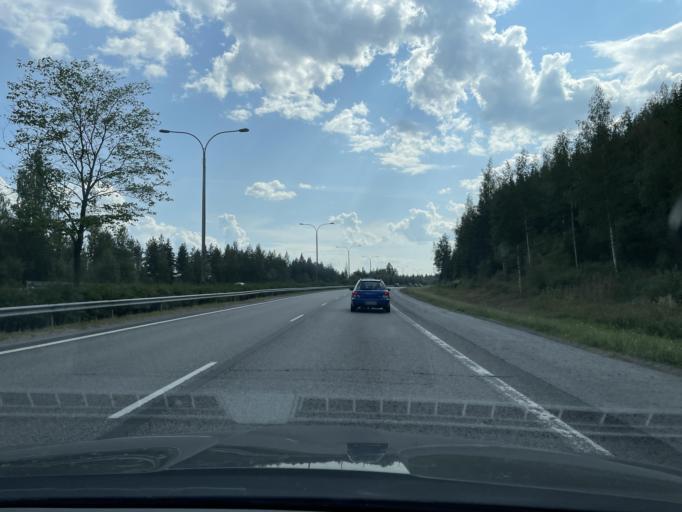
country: FI
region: Central Finland
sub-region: Jyvaeskylae
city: Jyvaeskylae
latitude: 62.1998
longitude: 25.7094
